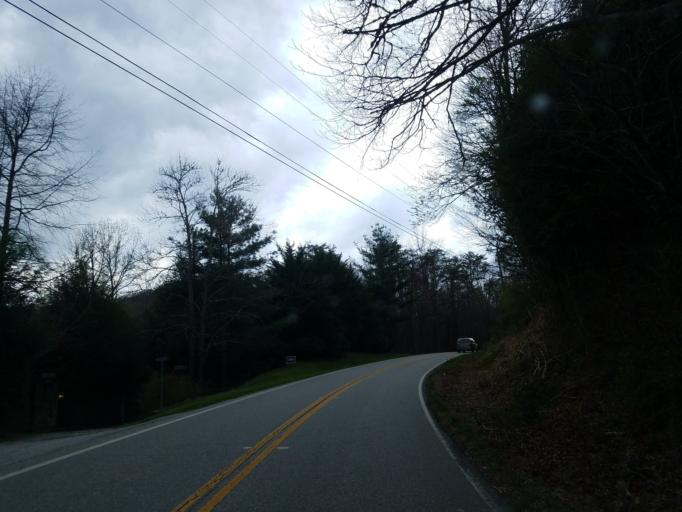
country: US
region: Georgia
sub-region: Lumpkin County
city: Dahlonega
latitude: 34.6941
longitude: -84.0268
